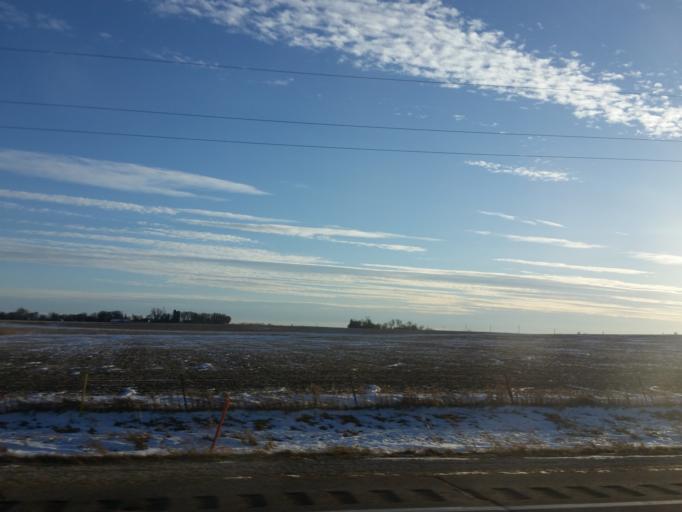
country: US
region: Iowa
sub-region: Butler County
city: Allison
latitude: 42.7450
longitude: -92.8726
